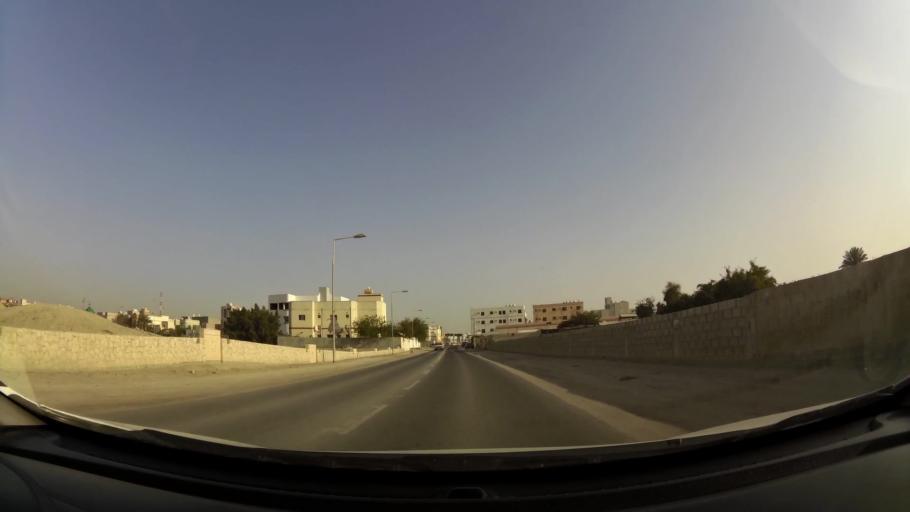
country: BH
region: Manama
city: Jidd Hafs
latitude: 26.2128
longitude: 50.5006
